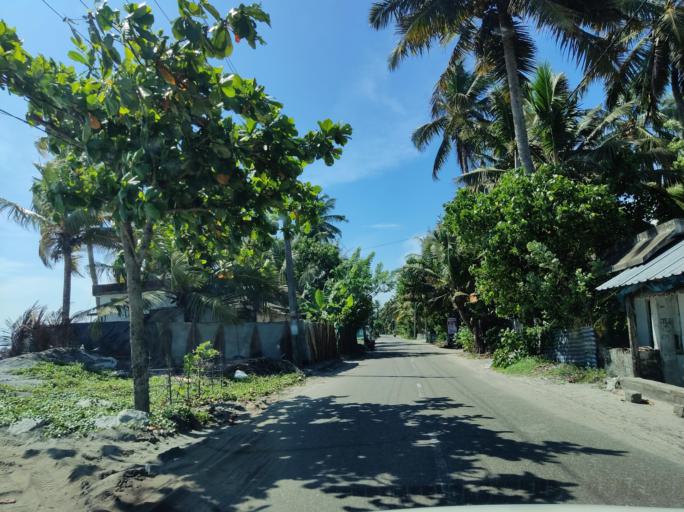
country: IN
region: Kerala
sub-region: Alappuzha
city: Kayankulam
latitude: 9.1936
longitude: 76.4375
